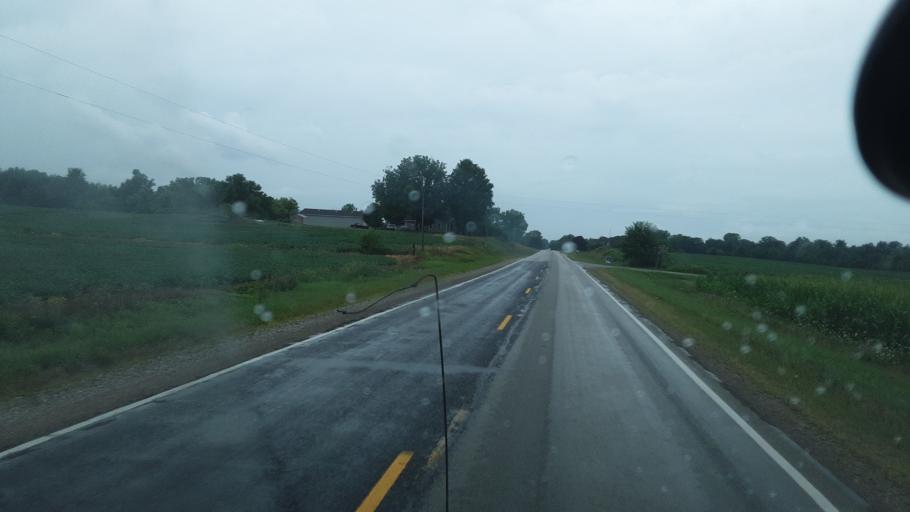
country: US
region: Indiana
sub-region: Steuben County
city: Hamilton
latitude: 41.5591
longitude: -84.8253
